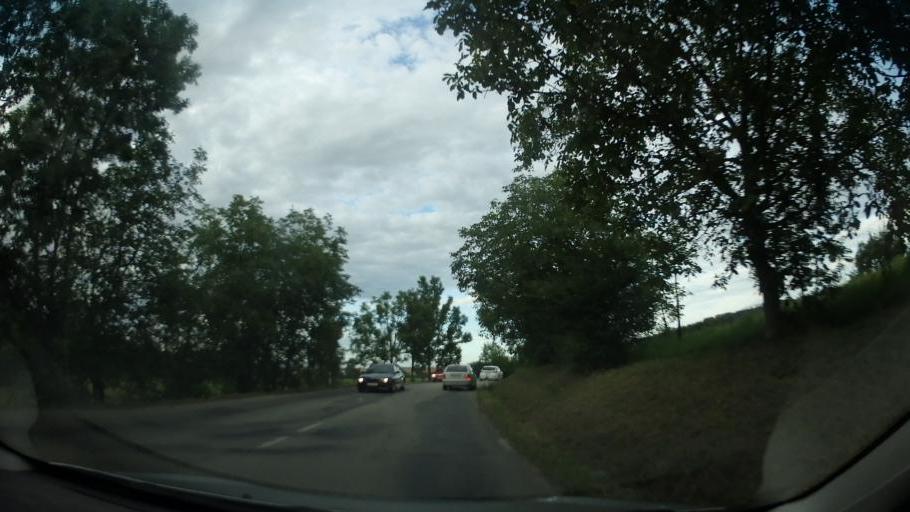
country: CZ
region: South Moravian
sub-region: Okres Blansko
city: Boskovice
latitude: 49.5417
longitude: 16.7030
